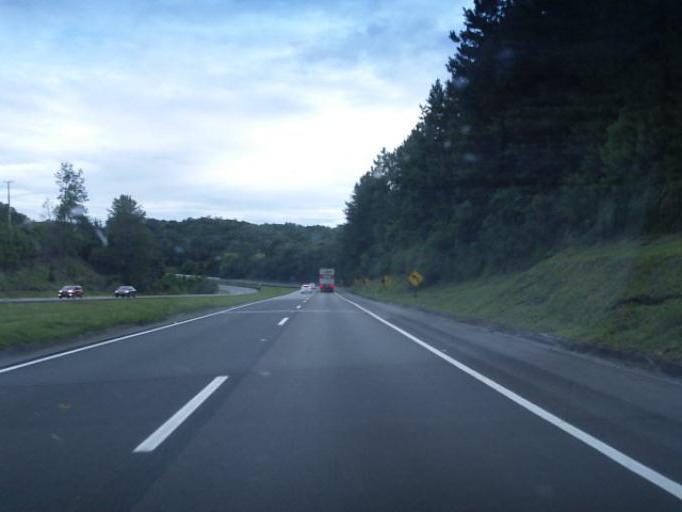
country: BR
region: Parana
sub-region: Campina Grande Do Sul
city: Campina Grande do Sul
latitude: -25.1993
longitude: -48.8951
